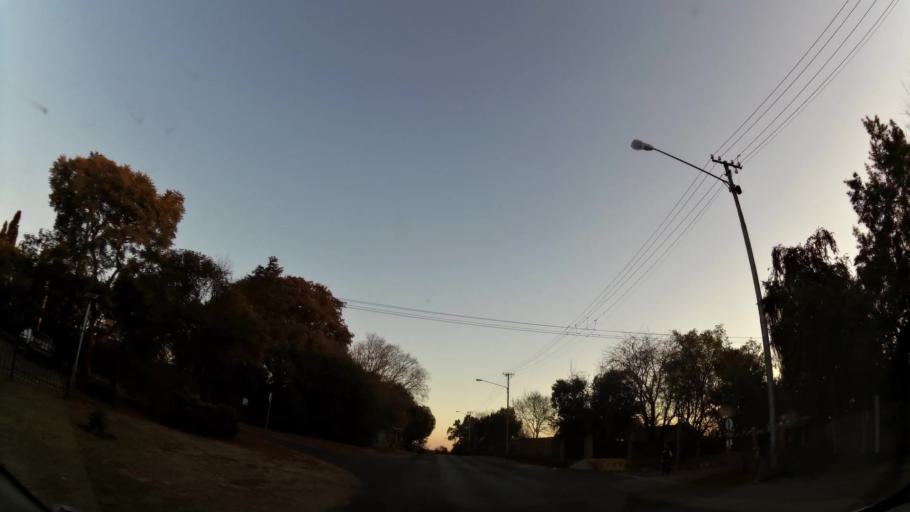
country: ZA
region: Gauteng
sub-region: City of Tshwane Metropolitan Municipality
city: Centurion
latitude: -25.8411
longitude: 28.1503
